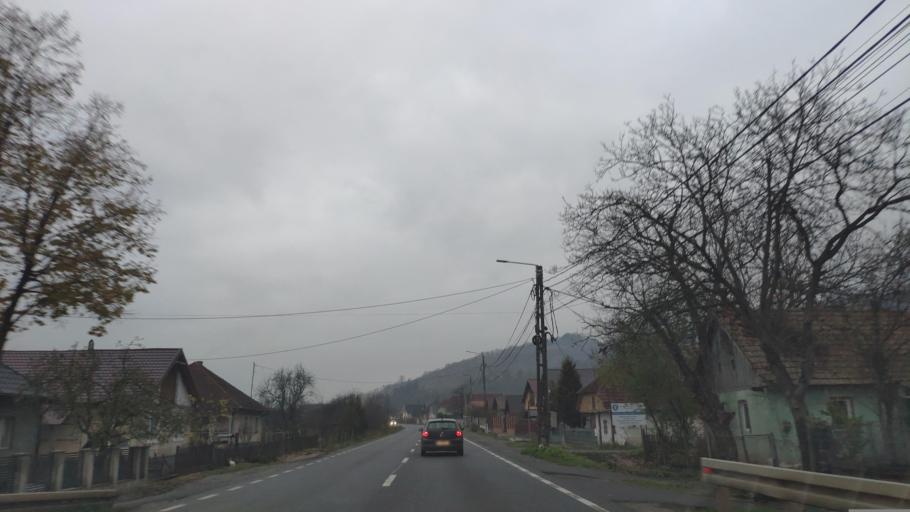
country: RO
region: Maramures
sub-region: Comuna Cicarlau
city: Ilba
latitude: 47.7113
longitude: 23.3633
